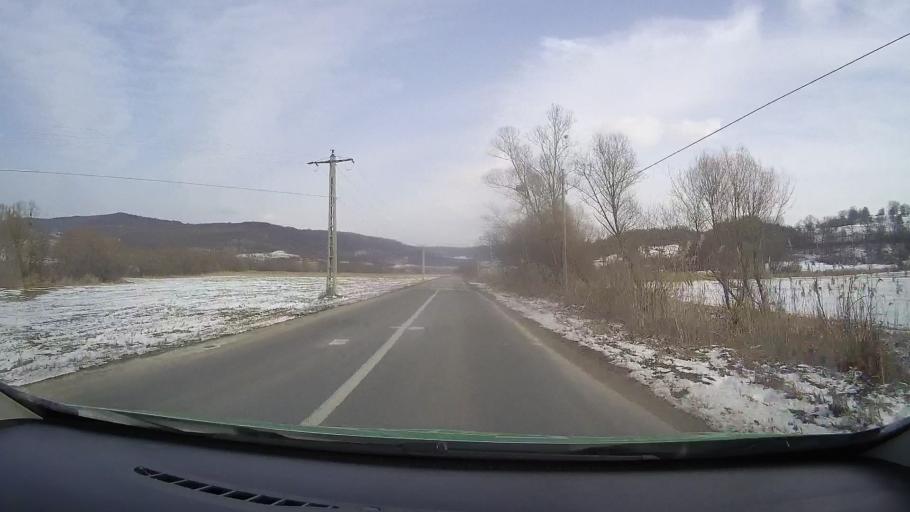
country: RO
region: Mures
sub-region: Comuna Apold
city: Apold
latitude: 46.1417
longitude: 24.8002
